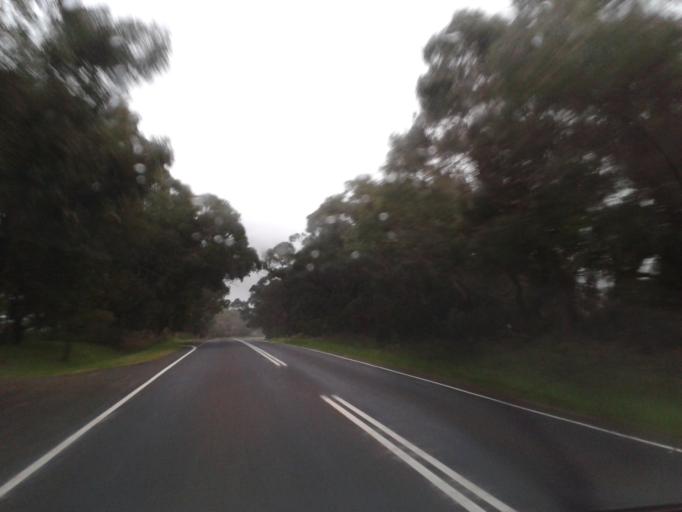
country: AU
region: Victoria
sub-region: Glenelg
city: Portland
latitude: -38.2390
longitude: 141.4677
